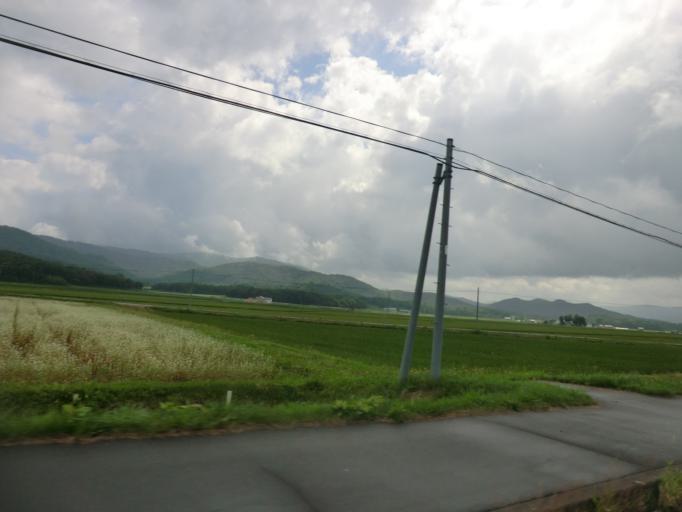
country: JP
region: Hokkaido
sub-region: Asahikawa-shi
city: Asahikawa
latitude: 44.0307
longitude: 142.1508
